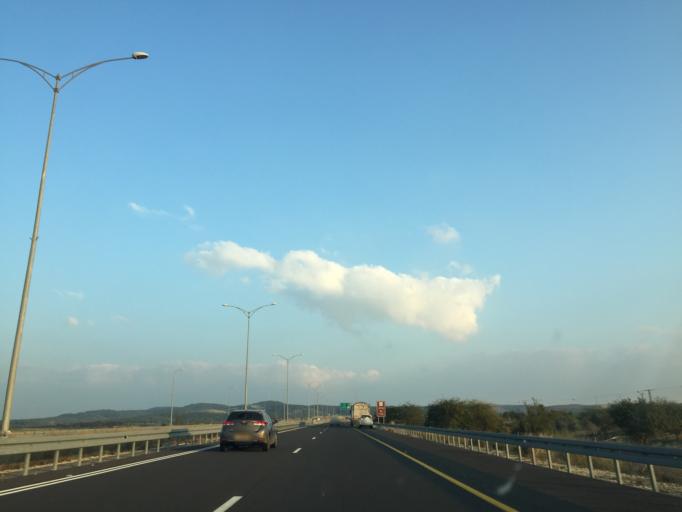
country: IL
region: Southern District
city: Lehavim
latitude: 31.3858
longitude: 34.8080
